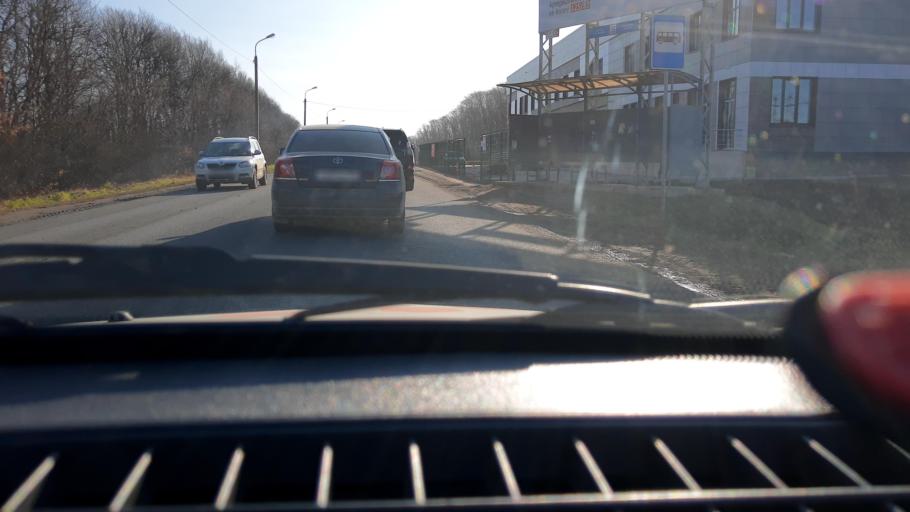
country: RU
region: Bashkortostan
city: Kabakovo
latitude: 54.6315
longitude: 56.0976
